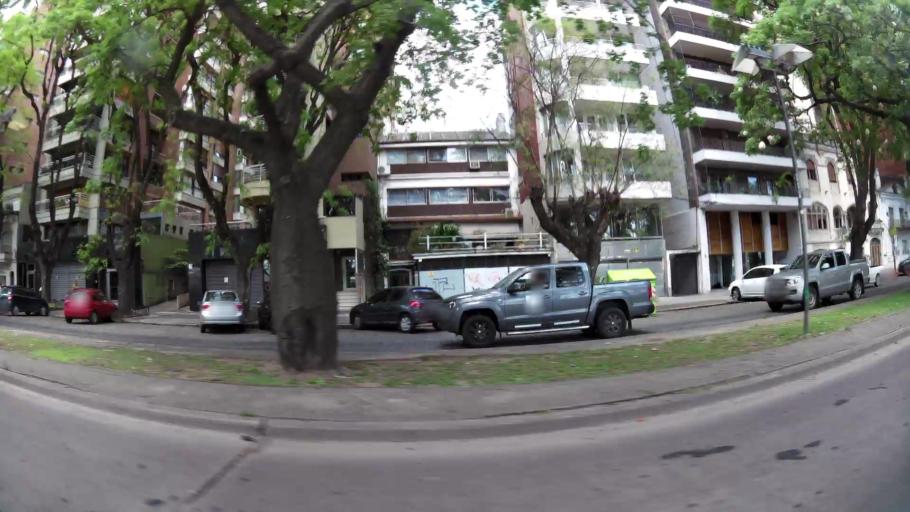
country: AR
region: Santa Fe
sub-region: Departamento de Rosario
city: Rosario
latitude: -32.9417
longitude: -60.6346
